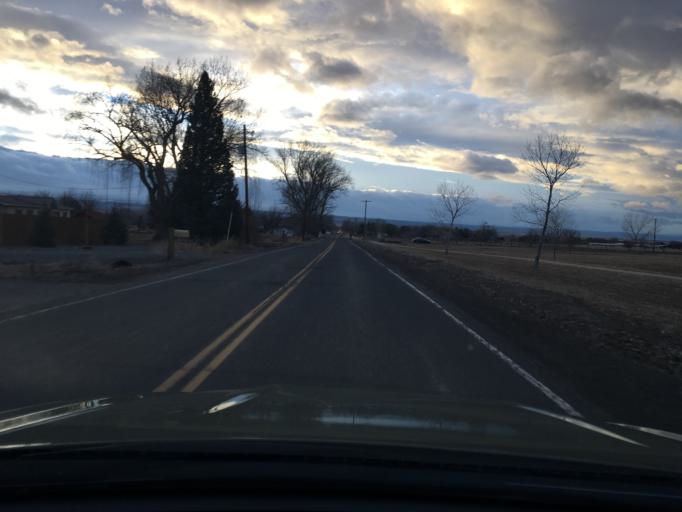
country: US
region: Colorado
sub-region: Montrose County
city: Montrose
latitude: 38.4817
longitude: -107.8369
